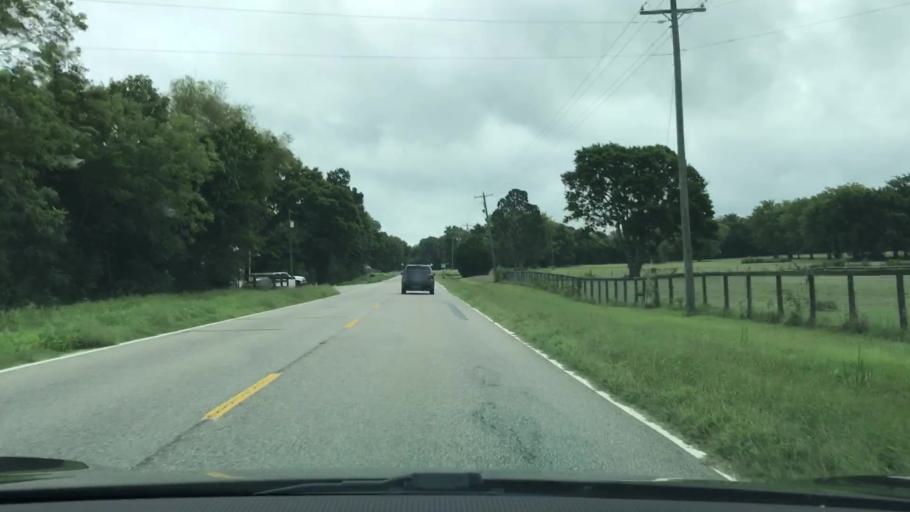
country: US
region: Alabama
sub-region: Montgomery County
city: Pike Road
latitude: 32.3027
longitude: -86.0566
